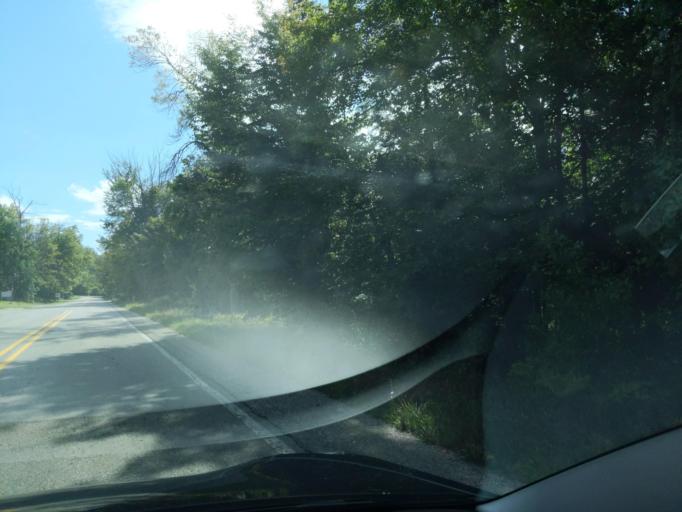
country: US
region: Michigan
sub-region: Antrim County
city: Bellaire
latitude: 45.0671
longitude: -85.3174
